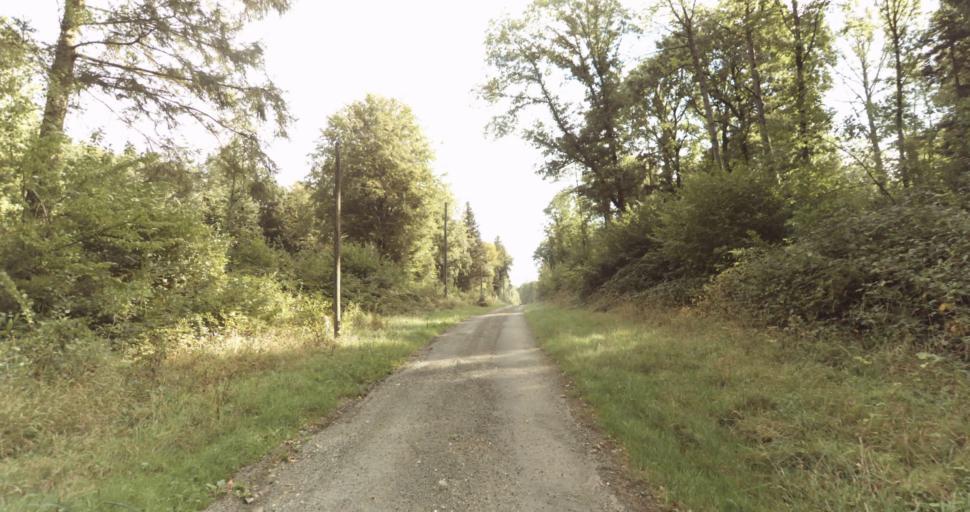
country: FR
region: Lower Normandy
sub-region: Departement de l'Orne
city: Gace
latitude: 48.8332
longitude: 0.2336
